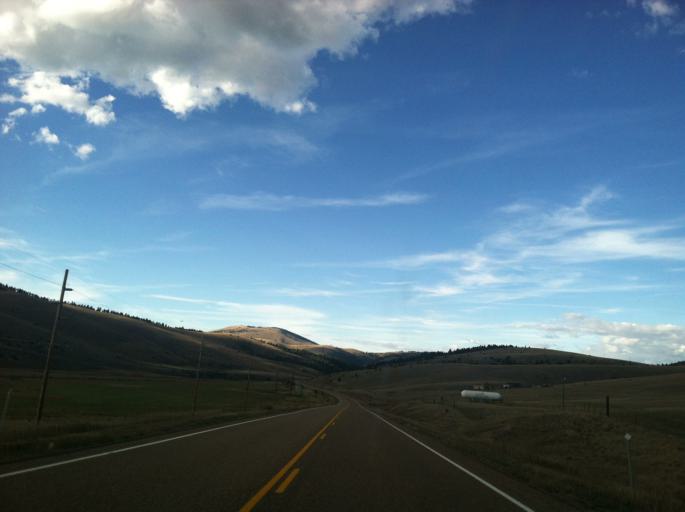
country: US
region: Montana
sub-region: Granite County
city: Philipsburg
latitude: 46.3734
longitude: -113.3132
